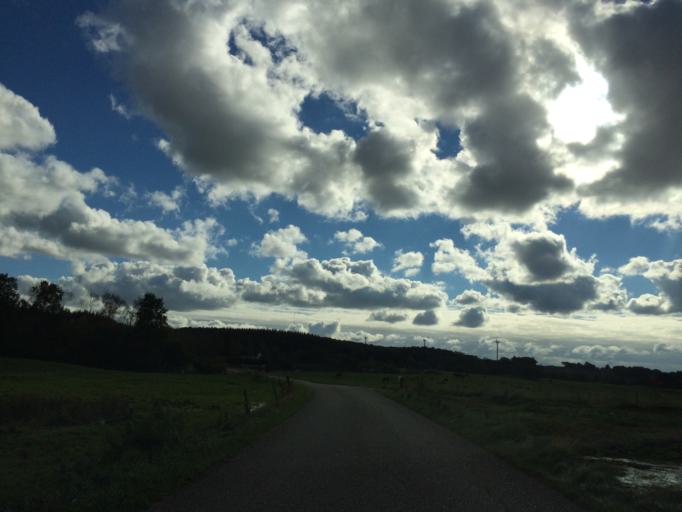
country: DK
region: Central Jutland
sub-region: Skanderborg Kommune
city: Ry
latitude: 56.1593
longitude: 9.7536
